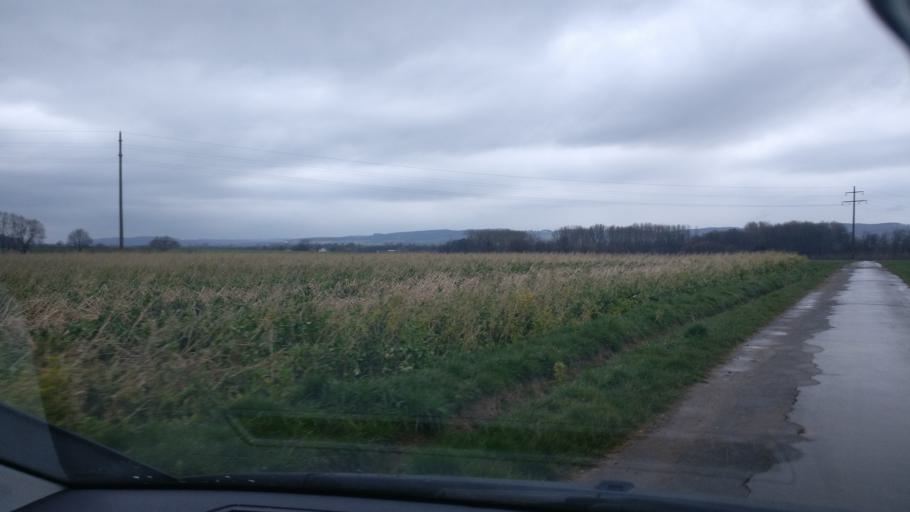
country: DE
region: North Rhine-Westphalia
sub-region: Regierungsbezirk Detmold
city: Lage
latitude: 52.0215
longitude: 8.7939
